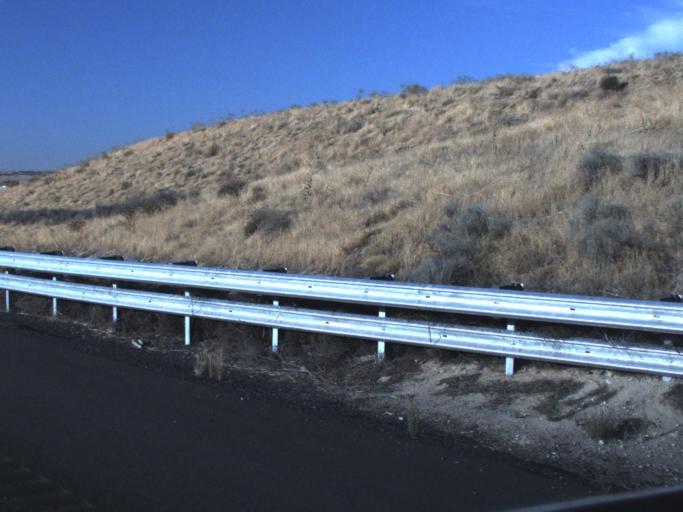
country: US
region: Washington
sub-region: Franklin County
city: Connell
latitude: 46.6901
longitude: -118.8390
